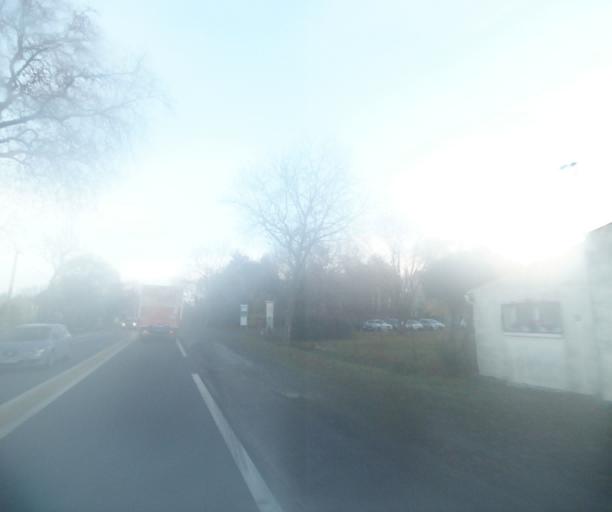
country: FR
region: Poitou-Charentes
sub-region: Departement de la Charente-Maritime
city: Fontcouverte
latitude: 45.7678
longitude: -0.5813
